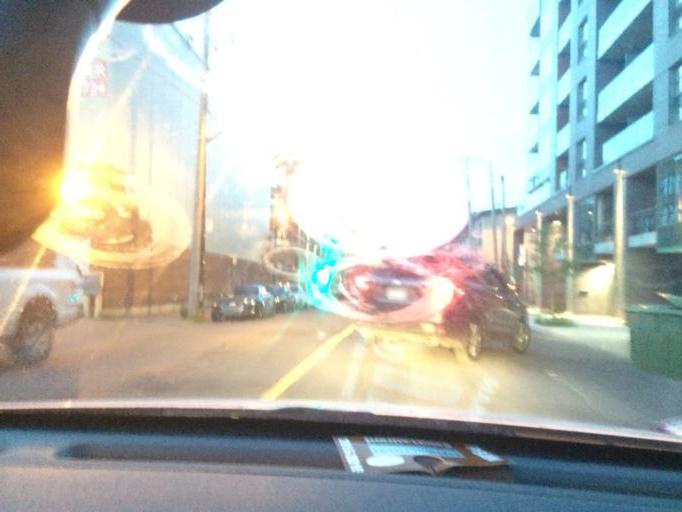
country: CA
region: Quebec
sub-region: Montreal
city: Montreal
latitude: 45.4865
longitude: -73.5678
